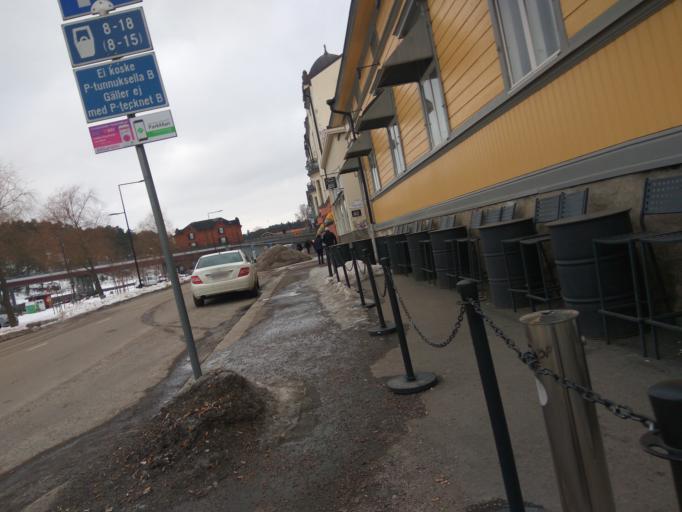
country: FI
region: Uusimaa
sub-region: Porvoo
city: Porvoo
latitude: 60.3927
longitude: 25.6599
